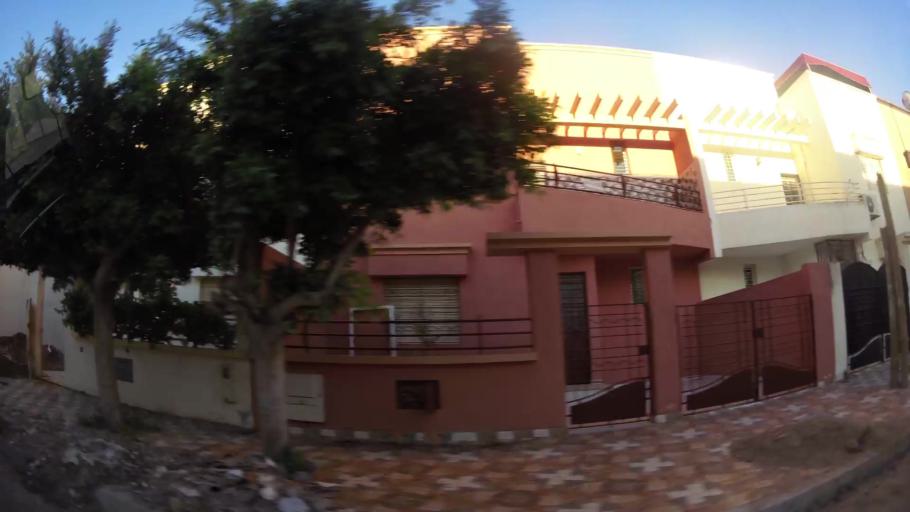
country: MA
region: Oriental
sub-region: Berkane-Taourirt
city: Madagh
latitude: 35.0798
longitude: -2.2393
